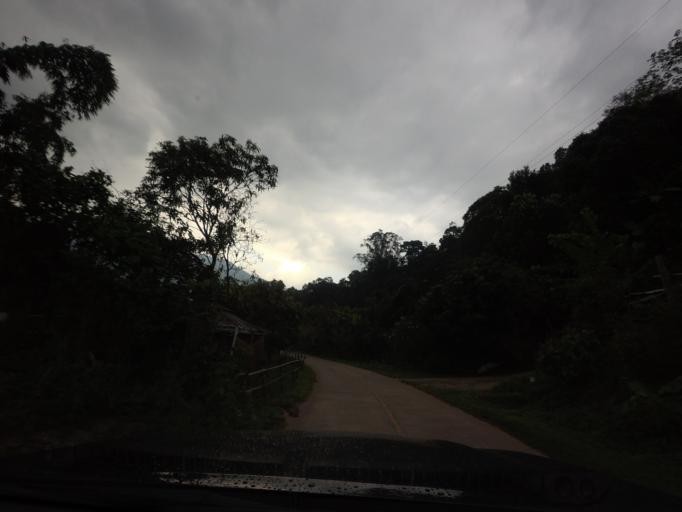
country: TH
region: Nan
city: Bo Kluea
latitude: 19.1929
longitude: 101.1962
